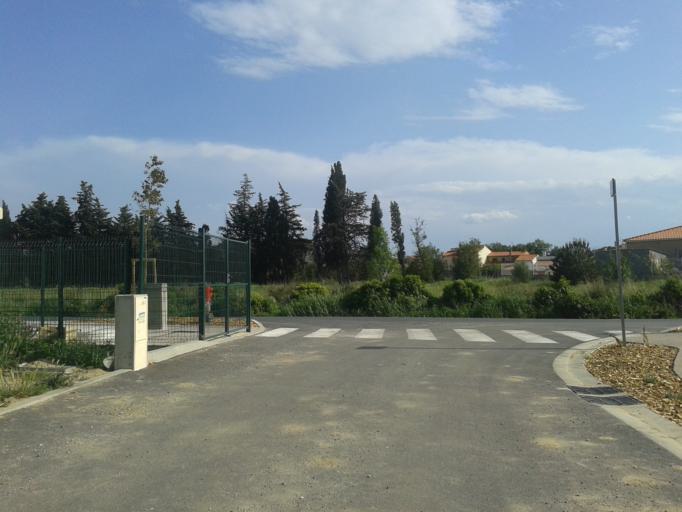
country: FR
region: Languedoc-Roussillon
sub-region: Departement des Pyrenees-Orientales
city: Pezilla-la-Riviere
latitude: 42.6966
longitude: 2.7780
